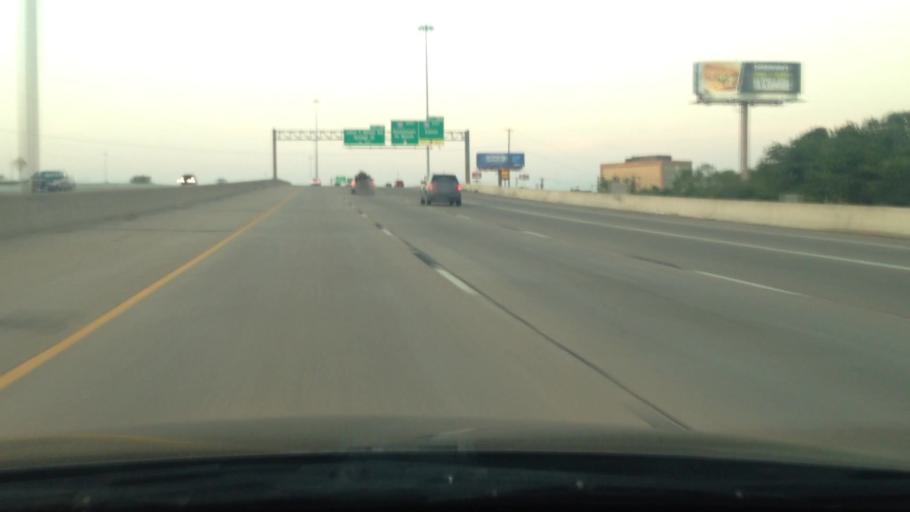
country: US
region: Texas
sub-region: Tarrant County
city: Richland Hills
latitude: 32.7515
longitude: -97.2185
